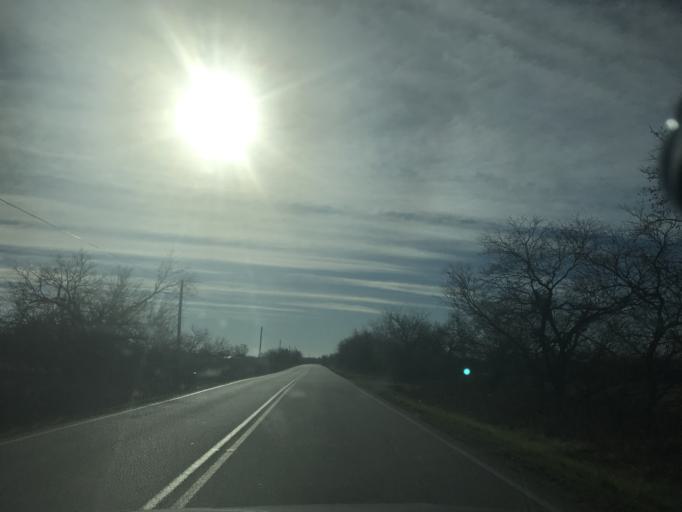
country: US
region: Texas
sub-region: Travis County
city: Manor
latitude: 30.2971
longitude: -97.5263
